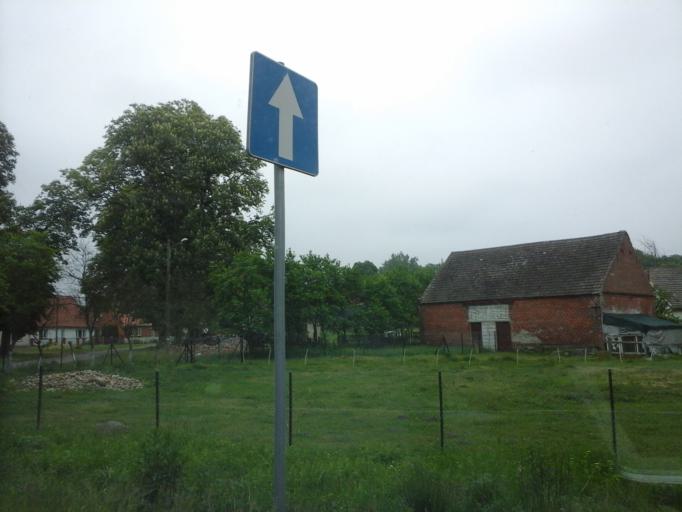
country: PL
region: West Pomeranian Voivodeship
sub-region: Powiat choszczenski
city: Pelczyce
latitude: 52.9386
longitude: 15.3556
